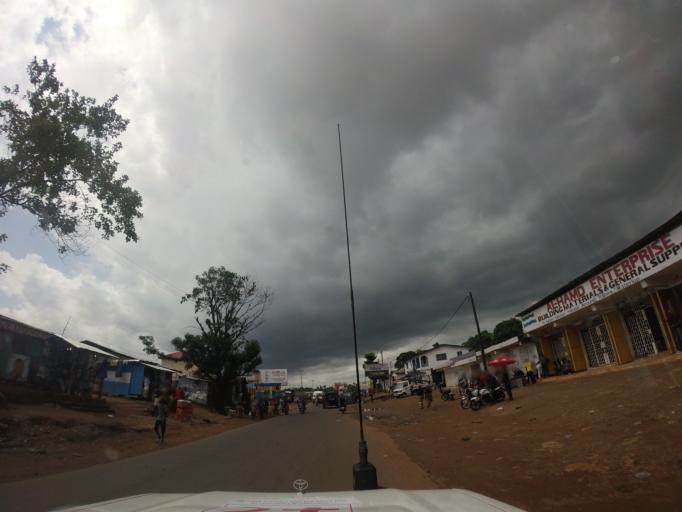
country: SL
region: Western Area
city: Waterloo
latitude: 8.3322
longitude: -13.0714
